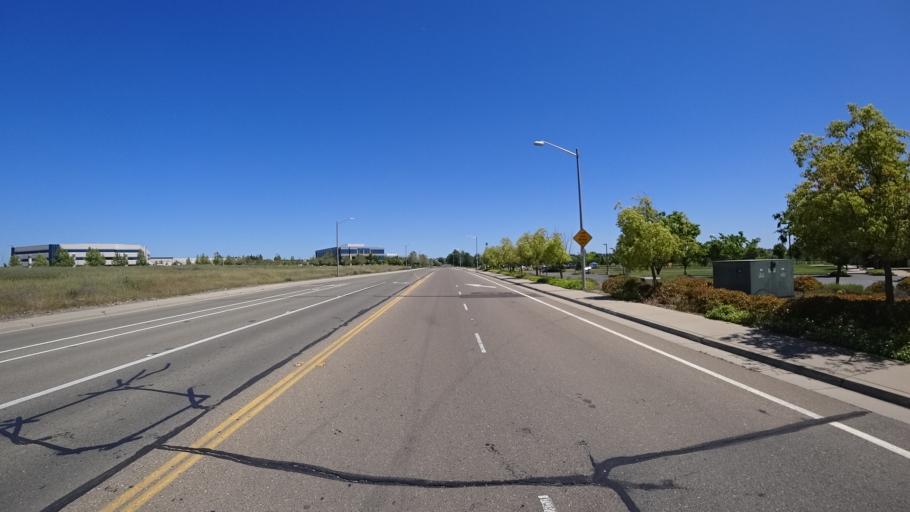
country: US
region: California
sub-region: Placer County
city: Roseville
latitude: 38.8102
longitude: -121.2923
